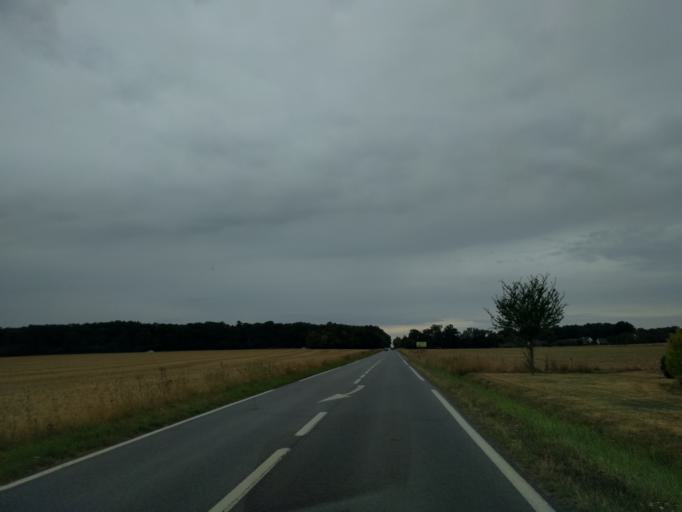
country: FR
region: Haute-Normandie
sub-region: Departement de l'Eure
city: Saint-Sebastien-de-Morsent
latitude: 49.0060
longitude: 1.0741
